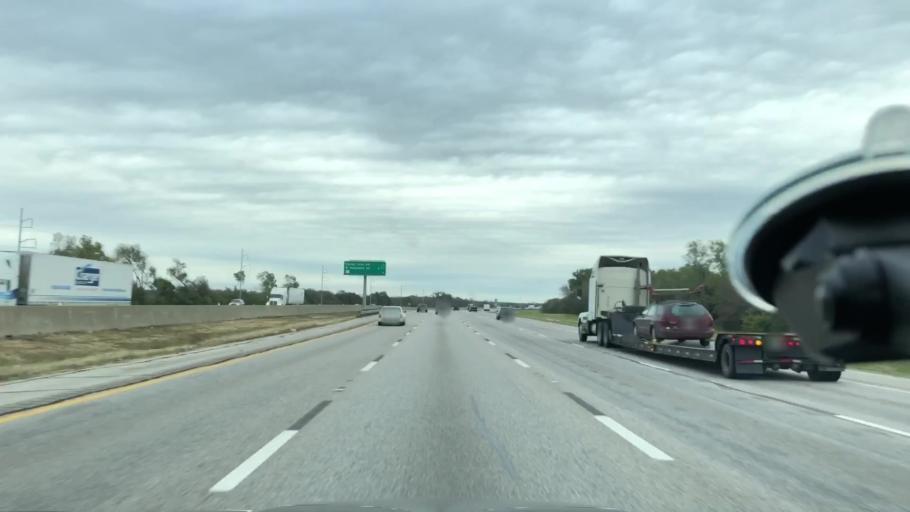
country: US
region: Texas
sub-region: Dallas County
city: Hutchins
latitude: 32.6727
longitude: -96.7047
